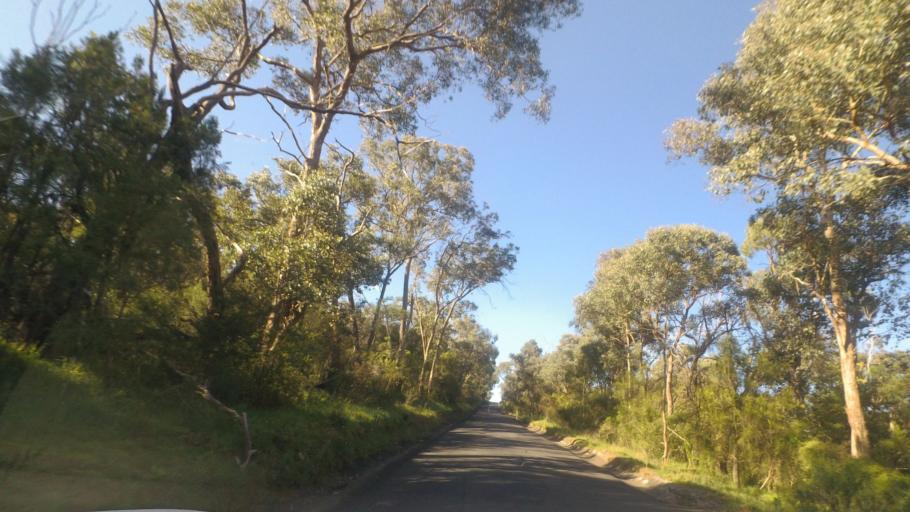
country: AU
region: Victoria
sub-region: Nillumbik
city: Research
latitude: -37.6906
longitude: 145.1732
